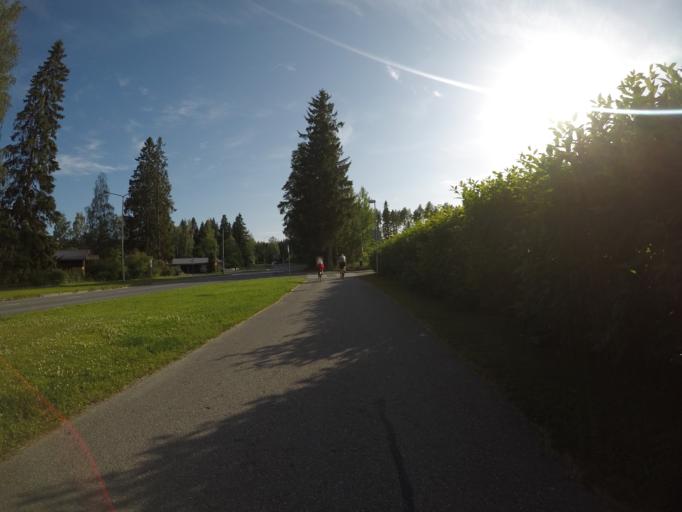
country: FI
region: Haeme
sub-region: Haemeenlinna
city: Haemeenlinna
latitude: 60.9749
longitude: 24.3931
